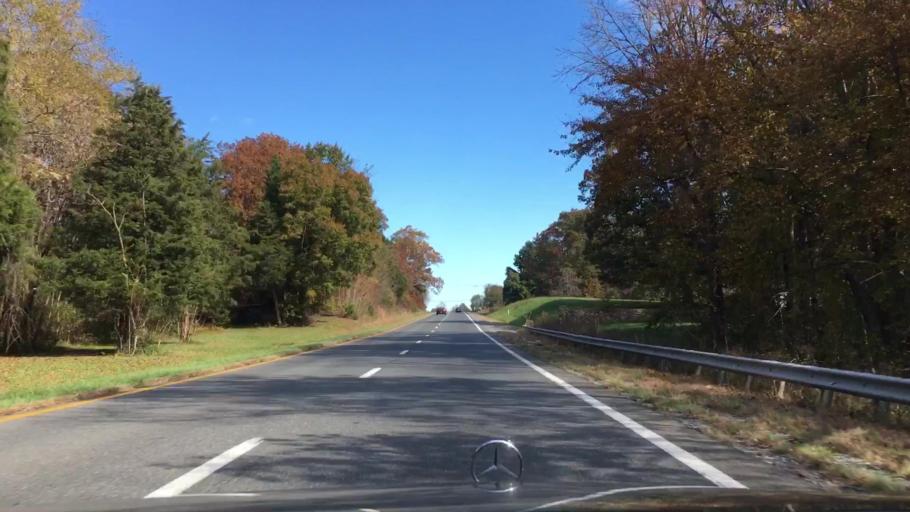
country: US
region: Virginia
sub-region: Campbell County
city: Altavista
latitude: 37.1613
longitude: -79.2200
